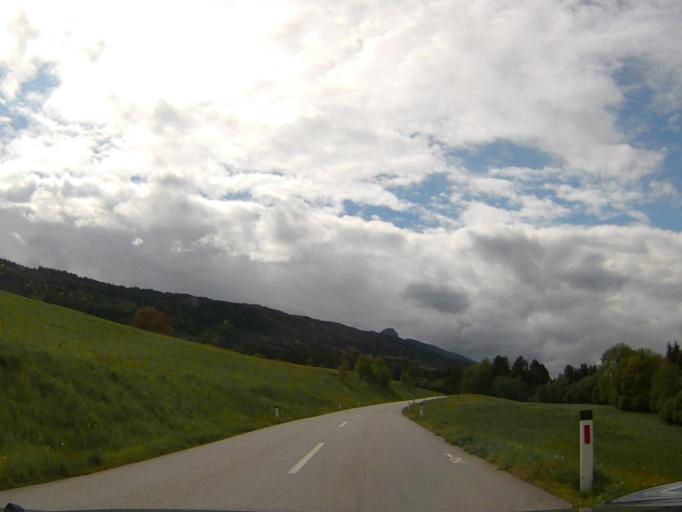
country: AT
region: Carinthia
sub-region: Politischer Bezirk Villach Land
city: Ferndorf
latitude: 46.7397
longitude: 13.5849
